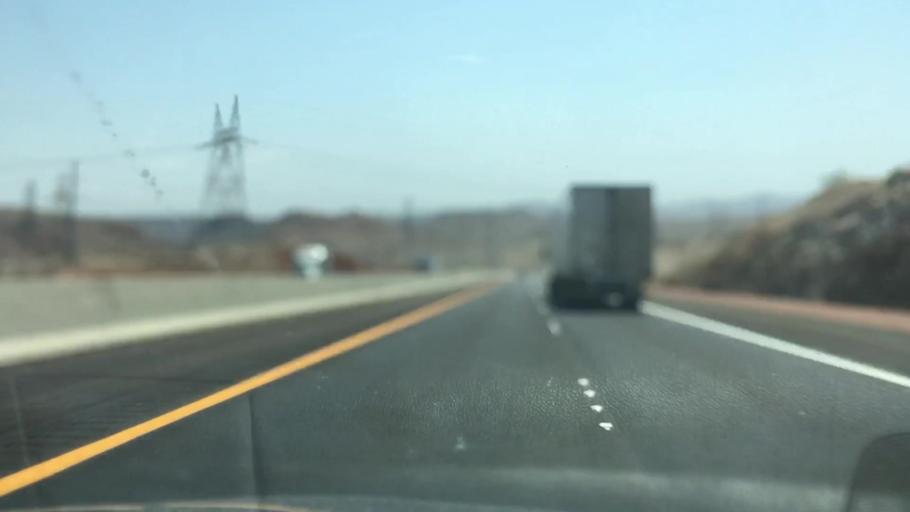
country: US
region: Nevada
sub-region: Clark County
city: Boulder City
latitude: 35.9849
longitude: -114.7953
